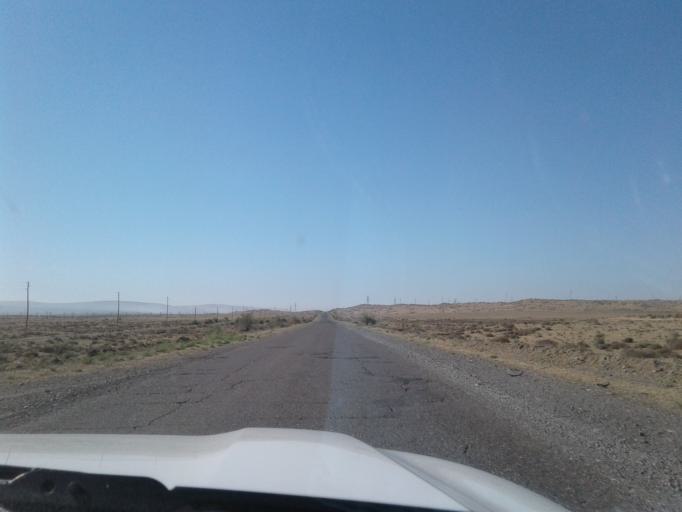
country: TM
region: Mary
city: Yoloeten
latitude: 36.5705
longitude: 62.5365
